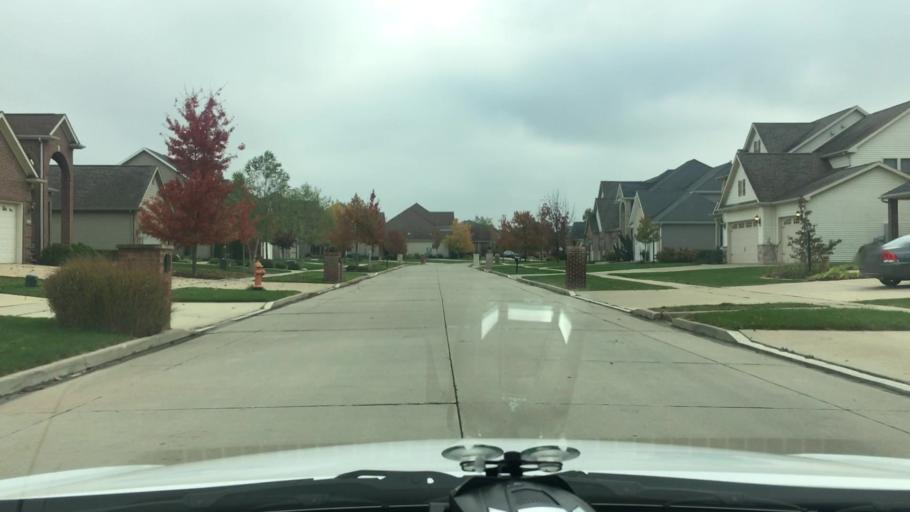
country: US
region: Illinois
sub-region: Champaign County
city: Savoy
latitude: 40.0947
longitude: -88.3260
